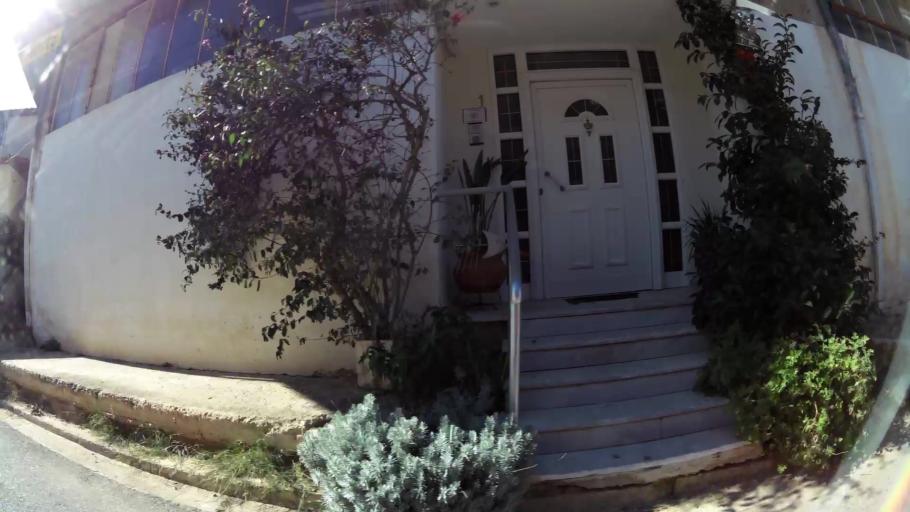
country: GR
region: Attica
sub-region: Nomarchia Anatolikis Attikis
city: Pikermi
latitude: 38.0016
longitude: 23.9383
